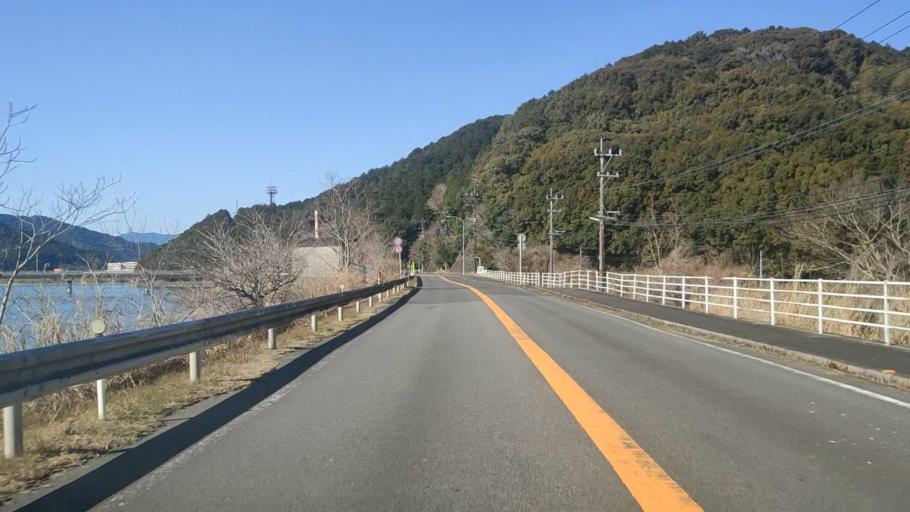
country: JP
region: Oita
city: Saiki
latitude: 32.9403
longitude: 131.9135
